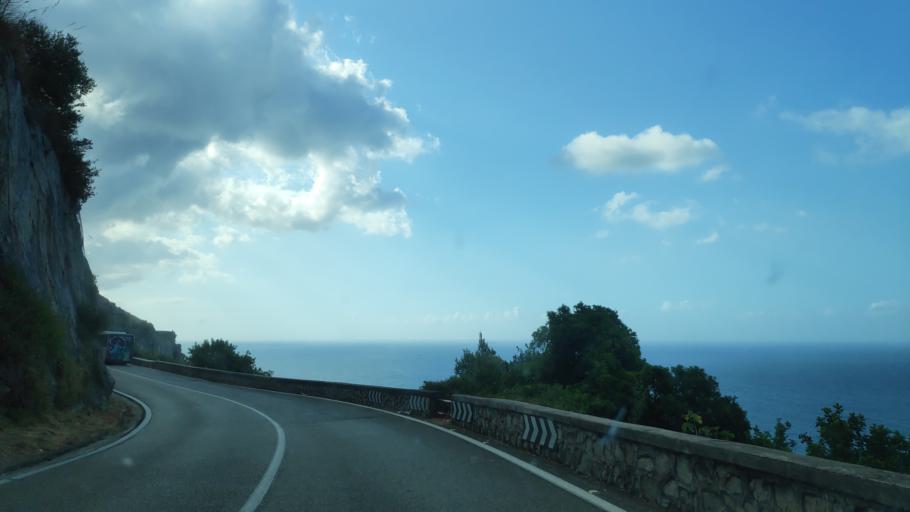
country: IT
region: Campania
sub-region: Provincia di Napoli
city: Arola-Preazzano
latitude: 40.6212
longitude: 14.4551
